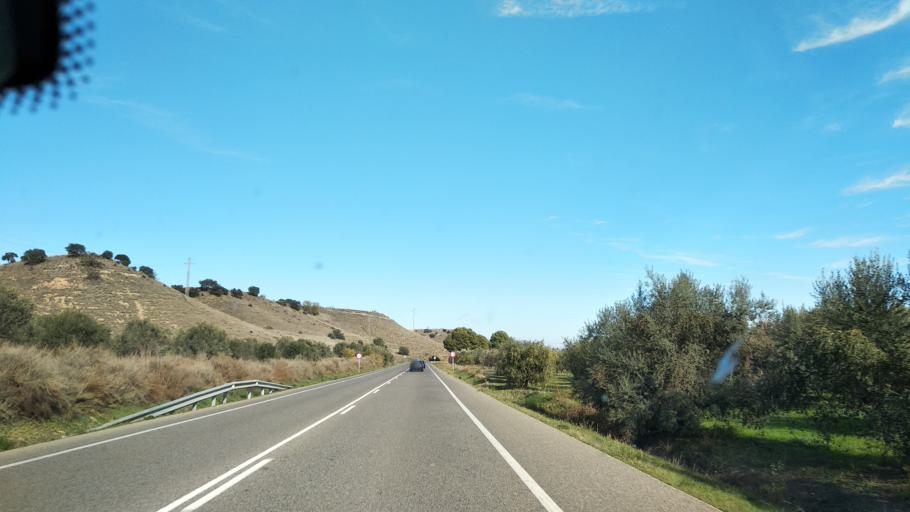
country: ES
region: Catalonia
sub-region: Provincia de Lleida
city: Vallfogona de Balaguer
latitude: 41.7606
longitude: 0.7753
